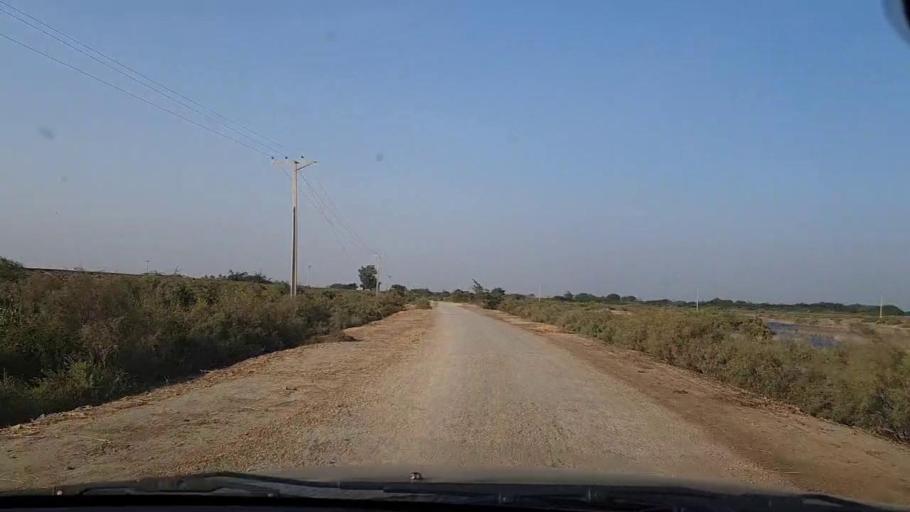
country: PK
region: Sindh
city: Chuhar Jamali
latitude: 24.2916
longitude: 67.7551
